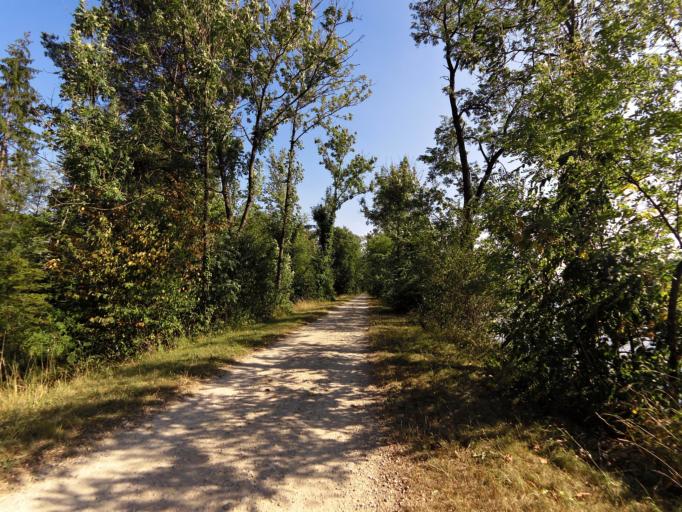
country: CH
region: Aargau
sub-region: Bezirk Brugg
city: Veltheim
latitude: 47.4298
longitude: 8.1635
